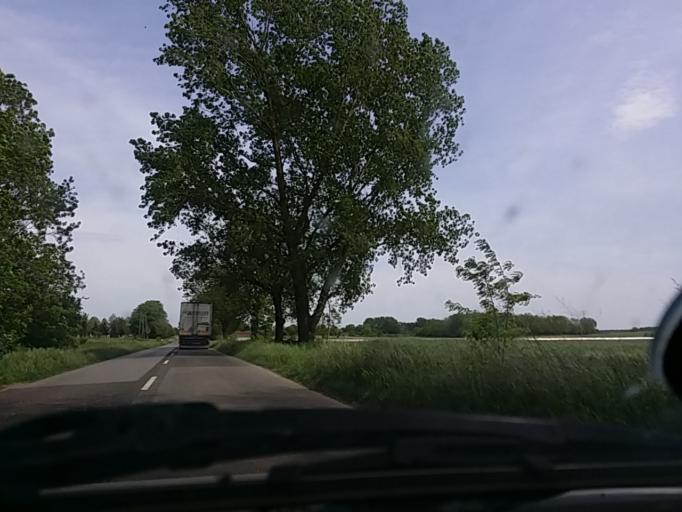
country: HU
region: Baranya
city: Vajszlo
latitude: 45.8647
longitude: 17.9708
